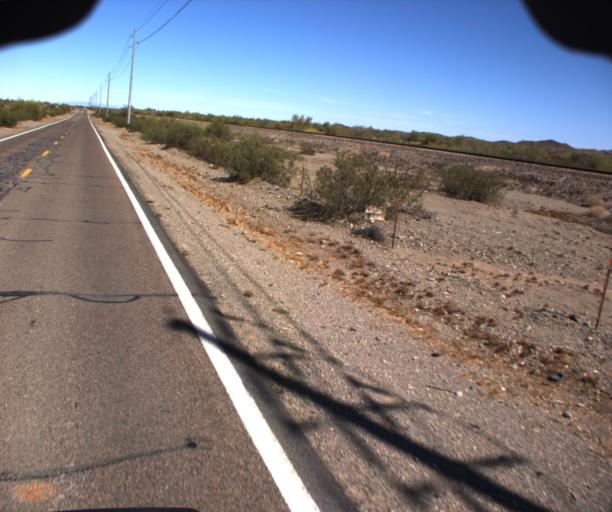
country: US
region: Arizona
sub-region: La Paz County
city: Salome
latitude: 33.7581
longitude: -113.7789
